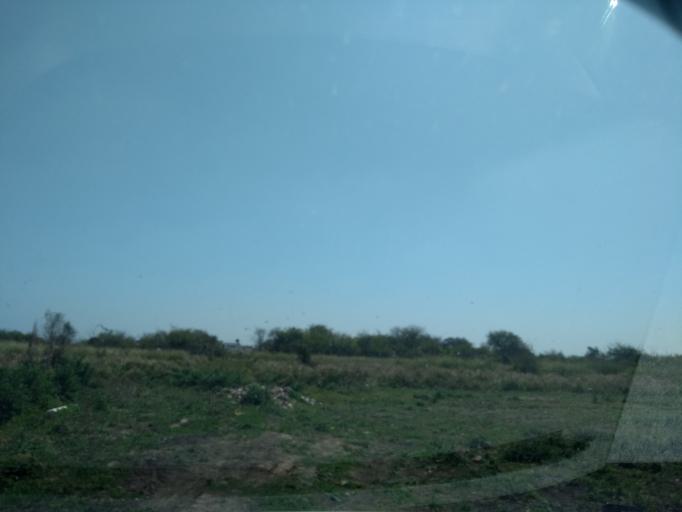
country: AR
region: Chaco
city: Resistencia
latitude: -27.4092
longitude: -58.9640
